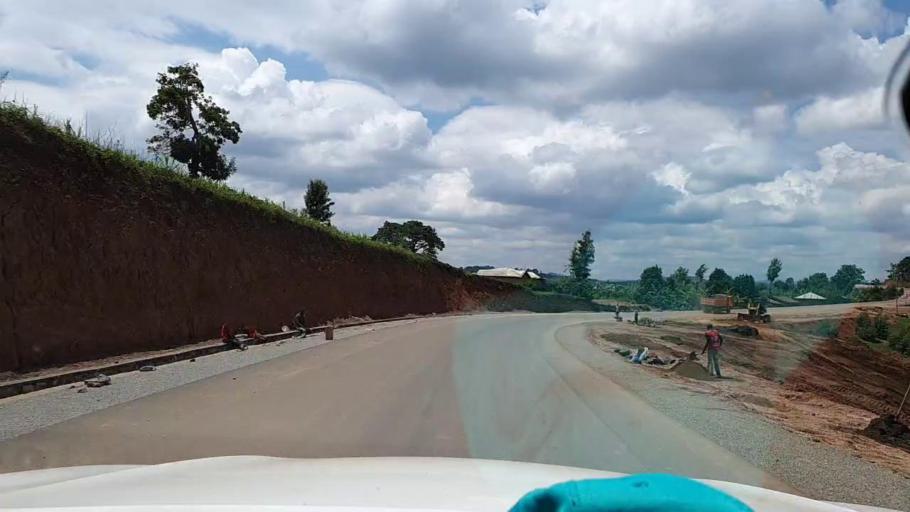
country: RW
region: Southern Province
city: Nzega
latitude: -2.6449
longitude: 29.5721
